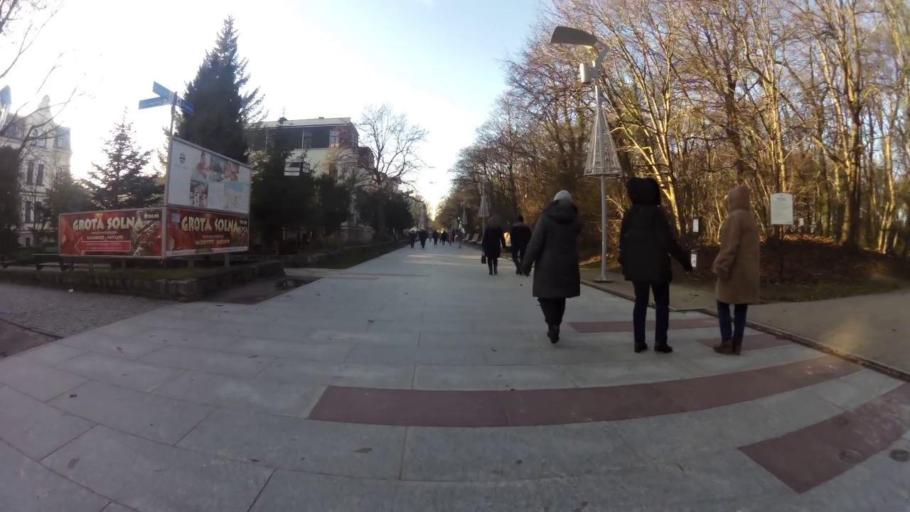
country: PL
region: West Pomeranian Voivodeship
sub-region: Powiat kolobrzeski
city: Kolobrzeg
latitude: 54.1846
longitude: 15.5725
